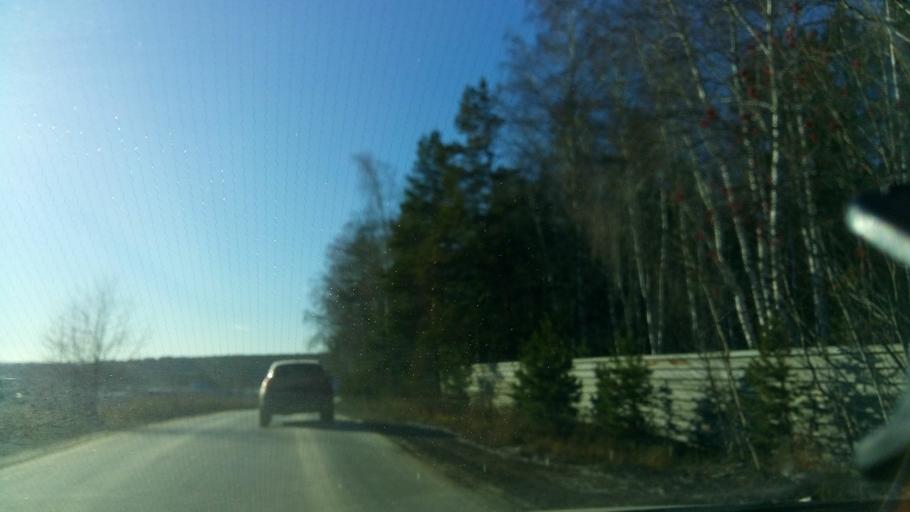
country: RU
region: Sverdlovsk
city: Gornyy Shchit
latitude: 56.7190
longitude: 60.5192
